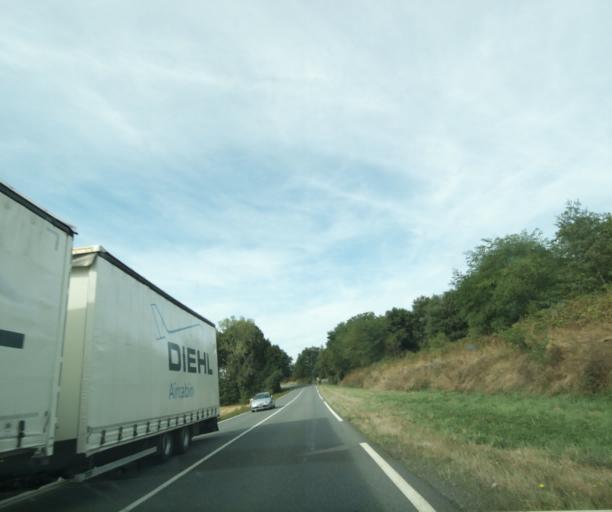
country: FR
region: Auvergne
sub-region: Departement de l'Allier
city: Saint-Gerand-le-Puy
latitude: 46.2121
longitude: 3.5408
